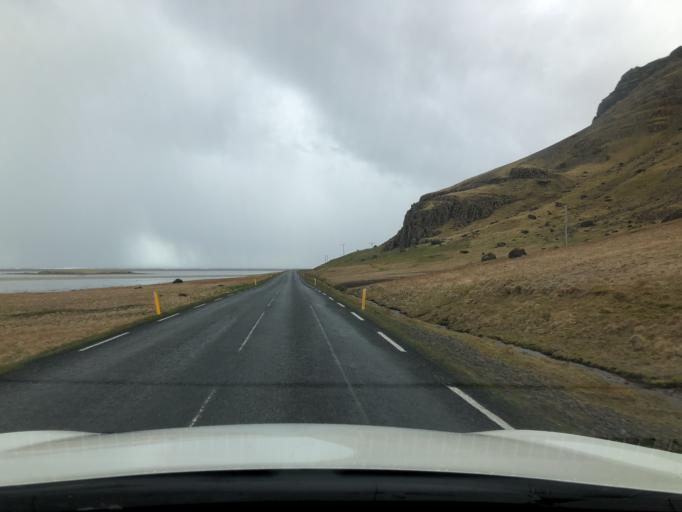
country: IS
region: East
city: Hoefn
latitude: 64.1893
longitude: -15.7478
